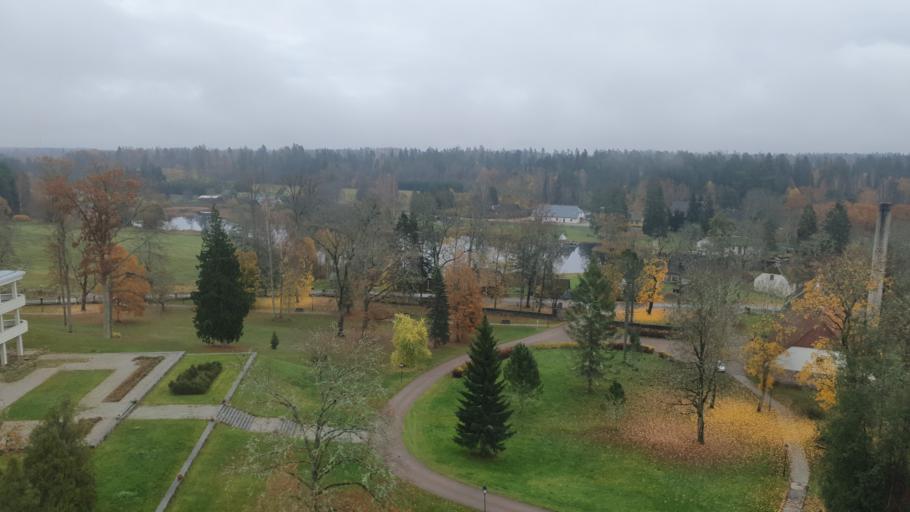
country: EE
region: Viljandimaa
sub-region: Karksi vald
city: Karksi-Nuia
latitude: 57.9932
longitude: 25.6652
